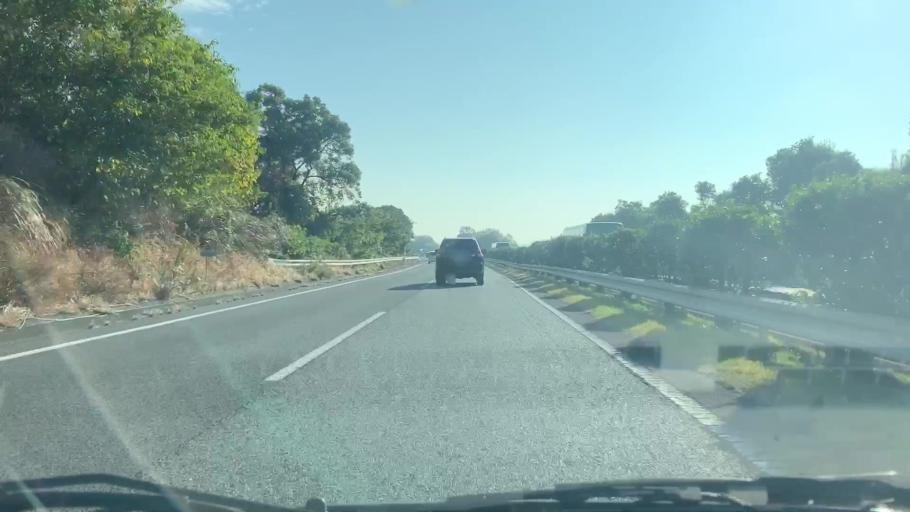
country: JP
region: Saga Prefecture
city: Saga-shi
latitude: 33.3080
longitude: 130.2262
